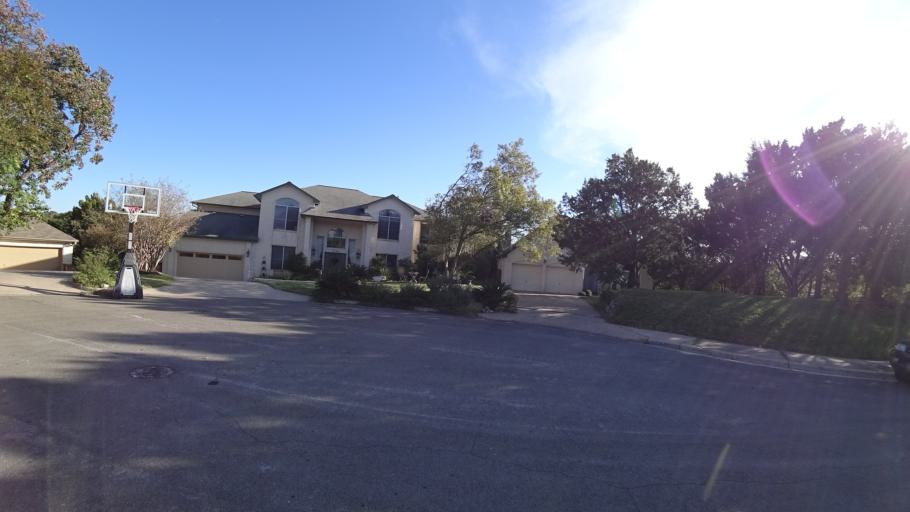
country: US
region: Texas
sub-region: Williamson County
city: Jollyville
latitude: 30.3949
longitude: -97.7751
